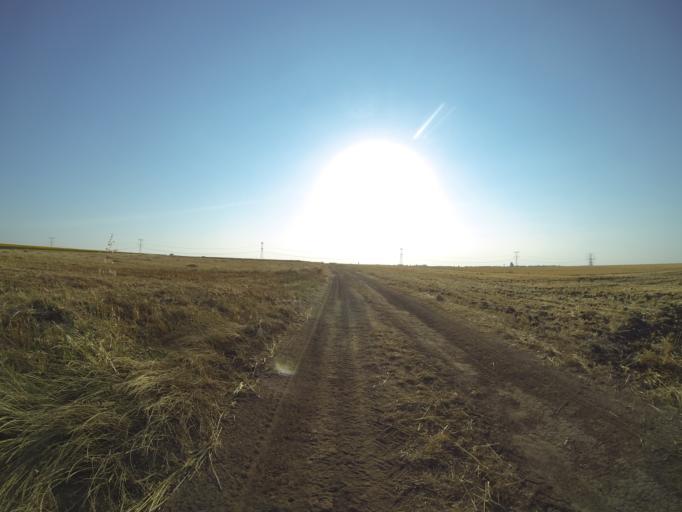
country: RO
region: Dolj
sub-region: Comuna Ceratu
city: Ceratu
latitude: 44.0283
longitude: 23.6721
